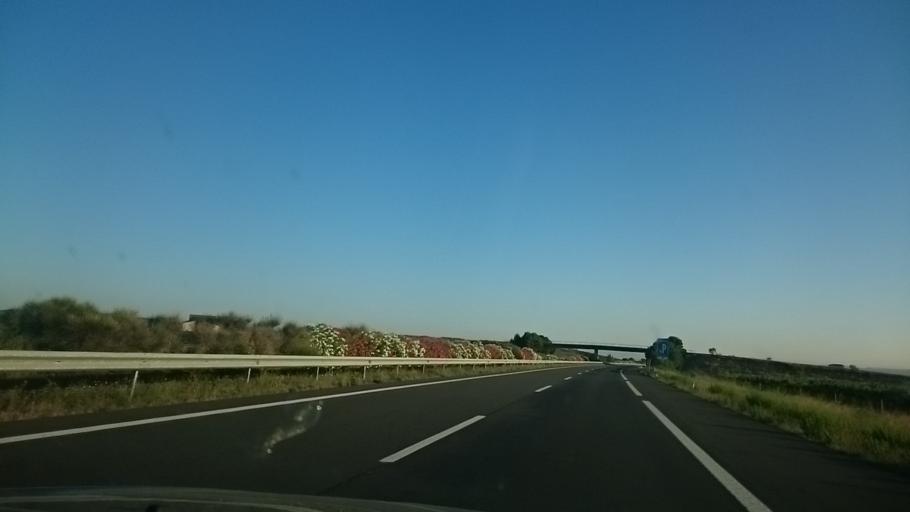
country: ES
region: La Rioja
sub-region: Provincia de La Rioja
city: Aldeanueva de Ebro
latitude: 42.2288
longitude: -1.8996
